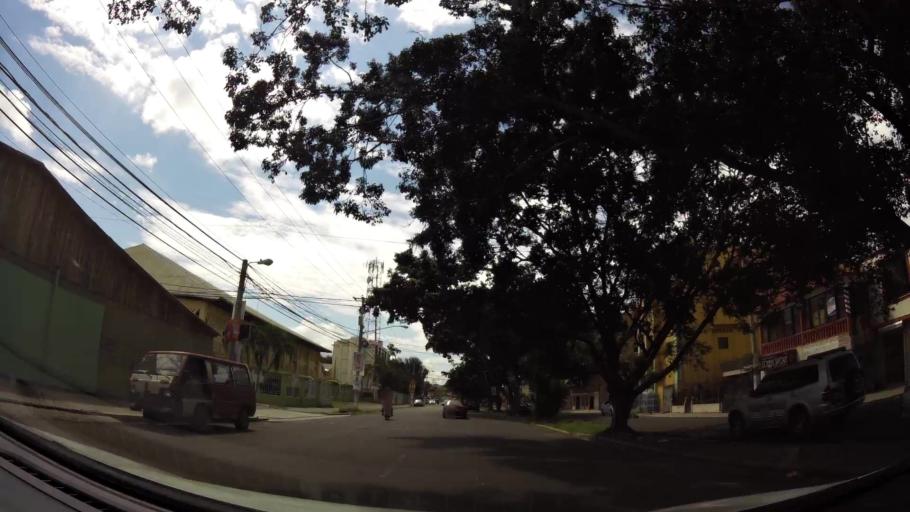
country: DO
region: Santiago
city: Santiago de los Caballeros
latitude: 19.4648
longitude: -70.7000
